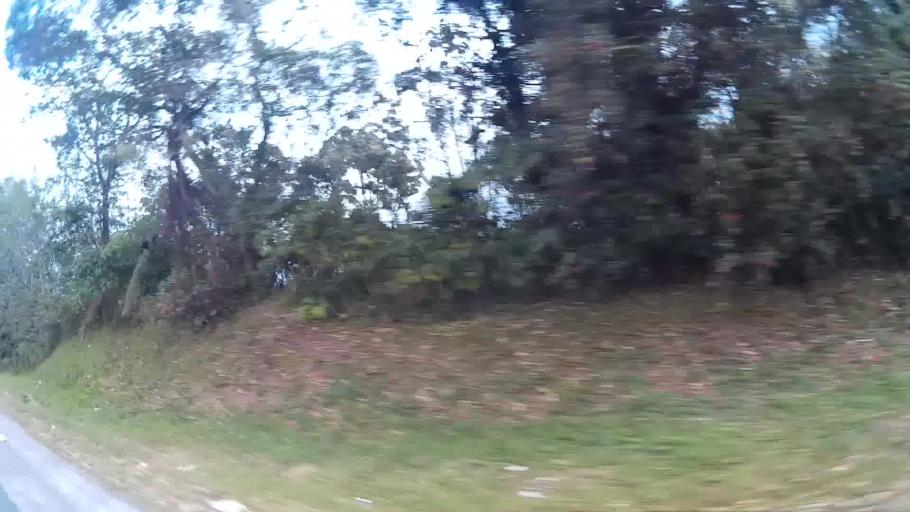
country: CO
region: Quindio
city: Filandia
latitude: 4.7232
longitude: -75.6256
